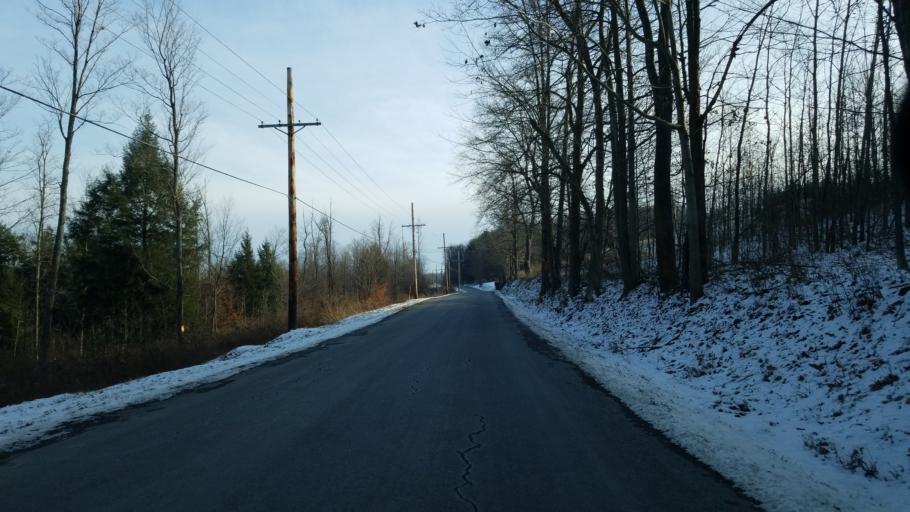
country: US
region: Pennsylvania
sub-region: Clearfield County
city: DuBois
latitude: 41.1185
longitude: -78.7091
